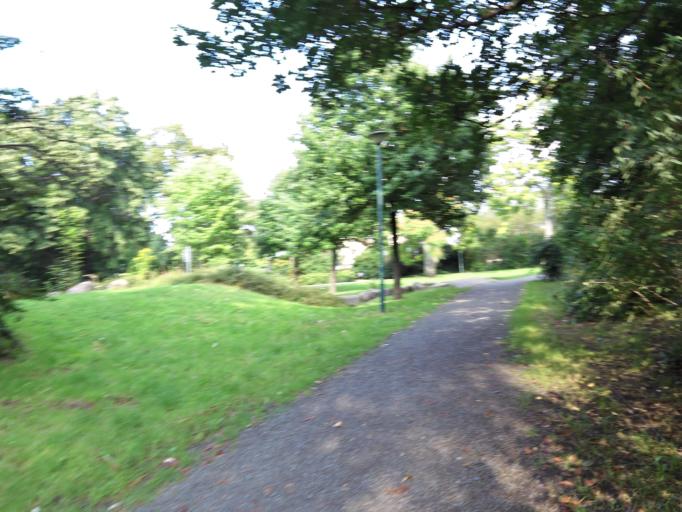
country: DE
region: Saxony
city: Leipzig
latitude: 51.3134
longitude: 12.3259
